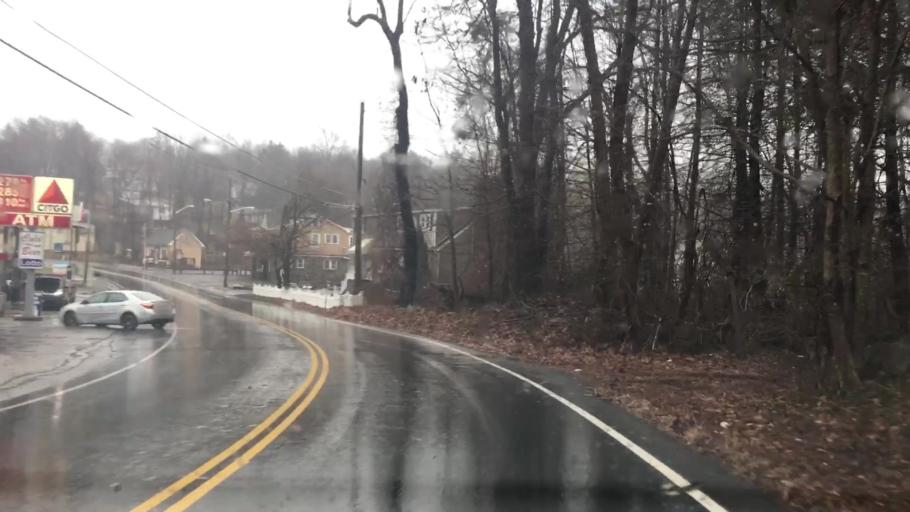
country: US
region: New York
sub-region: Putnam County
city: Putnam Lake
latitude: 41.4560
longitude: -73.5411
